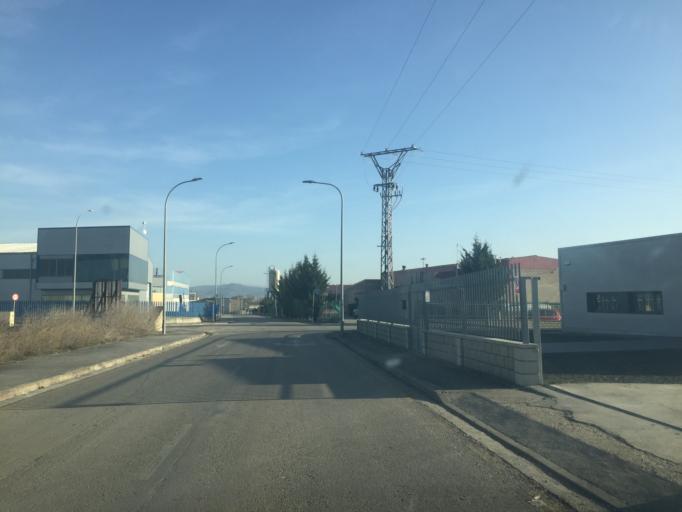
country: ES
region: Castille and Leon
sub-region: Provincia de Burgos
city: Medina de Pomar
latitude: 42.9239
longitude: -3.5823
